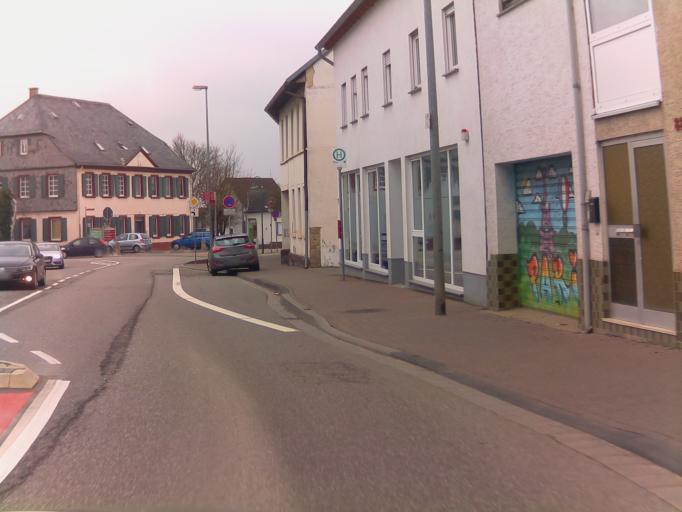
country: DE
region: Rheinland-Pfalz
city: Worrstadt
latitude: 49.8361
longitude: 8.1149
